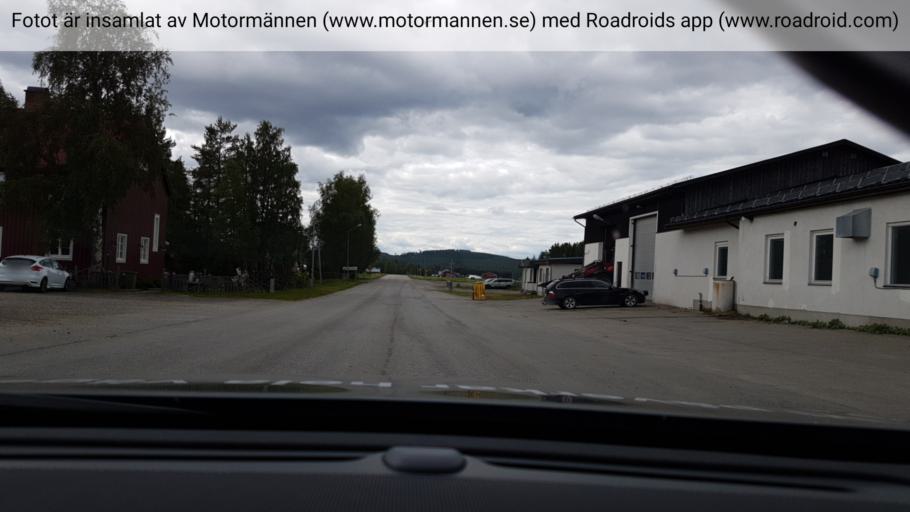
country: SE
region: Vaesterbotten
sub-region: Vindelns Kommun
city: Vindeln
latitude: 64.0906
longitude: 19.6601
